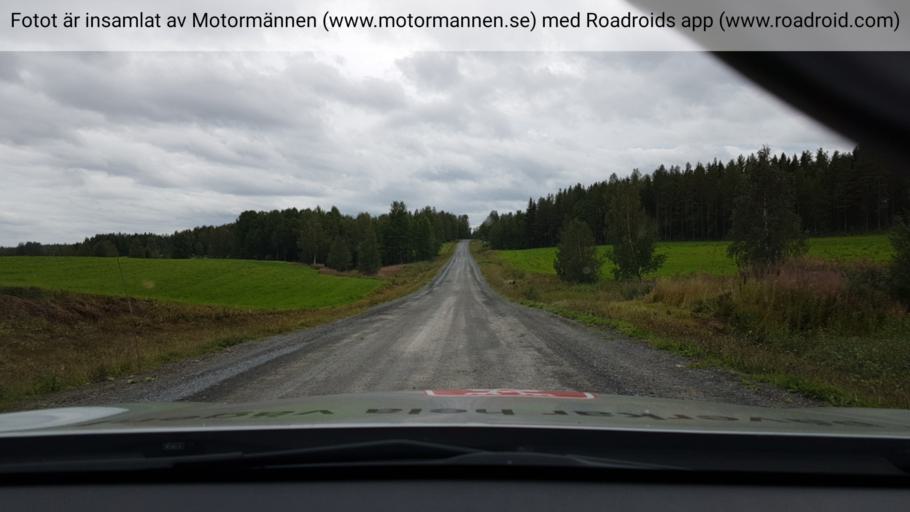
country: SE
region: Vaesterbotten
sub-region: Skelleftea Kommun
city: Forsbacka
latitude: 64.7892
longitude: 20.5102
